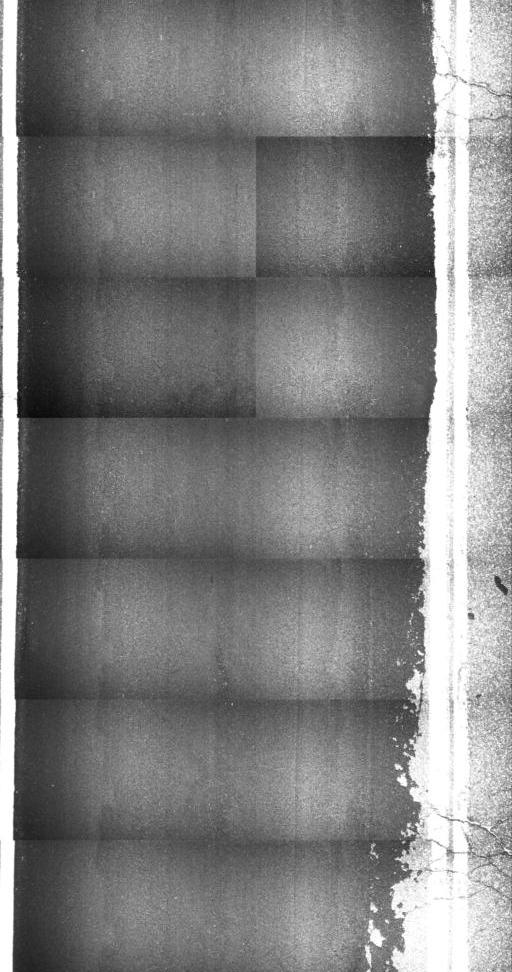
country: US
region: Vermont
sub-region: Lamoille County
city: Hyde Park
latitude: 44.6463
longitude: -72.5997
